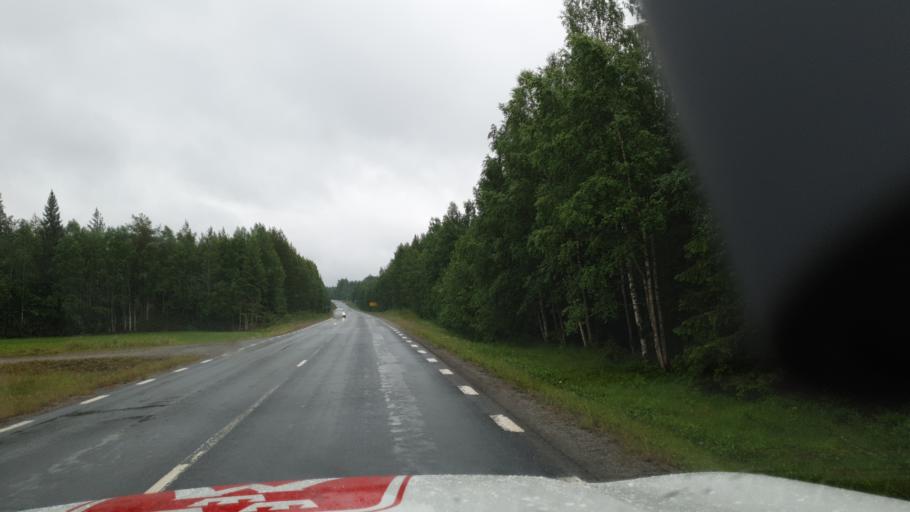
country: SE
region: Vaesterbotten
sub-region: Vannas Kommun
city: Vaennaes
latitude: 63.7720
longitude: 19.6922
